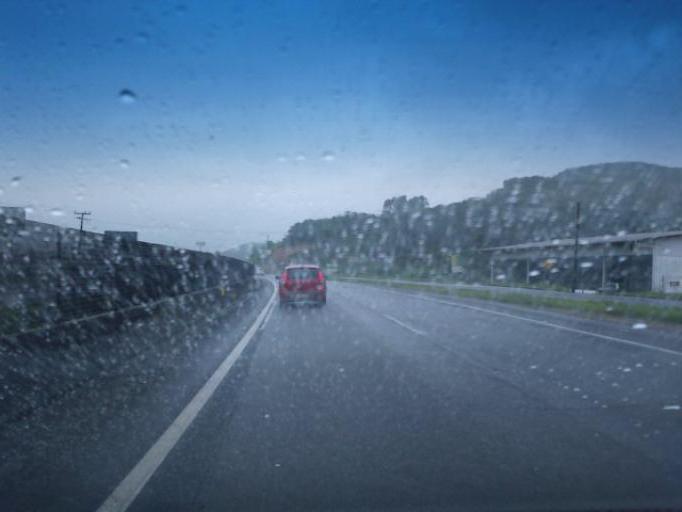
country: BR
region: Santa Catarina
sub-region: Penha
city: Penha
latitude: -26.8309
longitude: -48.6934
